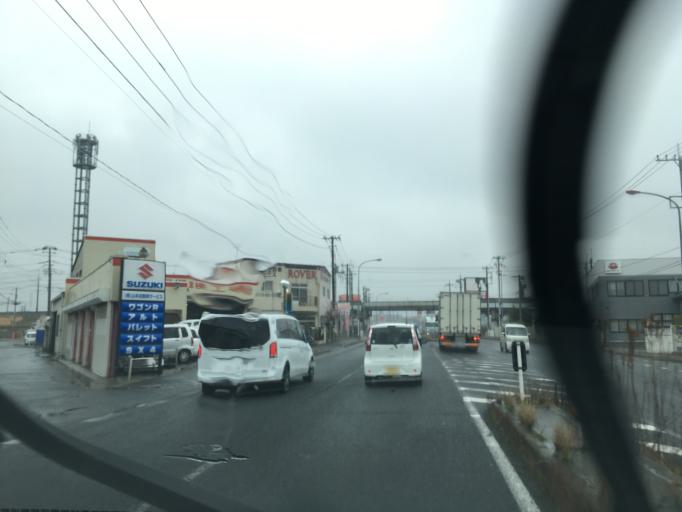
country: JP
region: Saitama
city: Koshigaya
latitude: 35.8749
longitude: 139.7779
